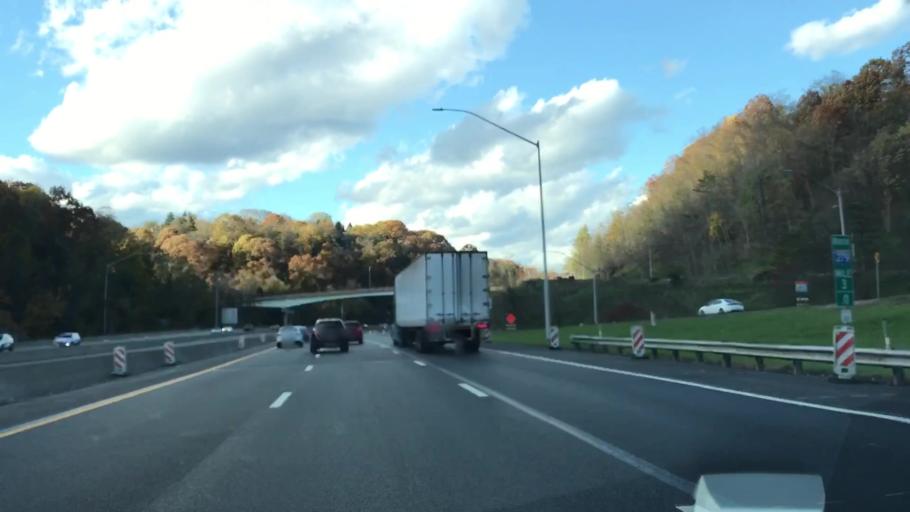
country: US
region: Pennsylvania
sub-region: Allegheny County
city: Millvale
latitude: 40.4742
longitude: -80.0059
